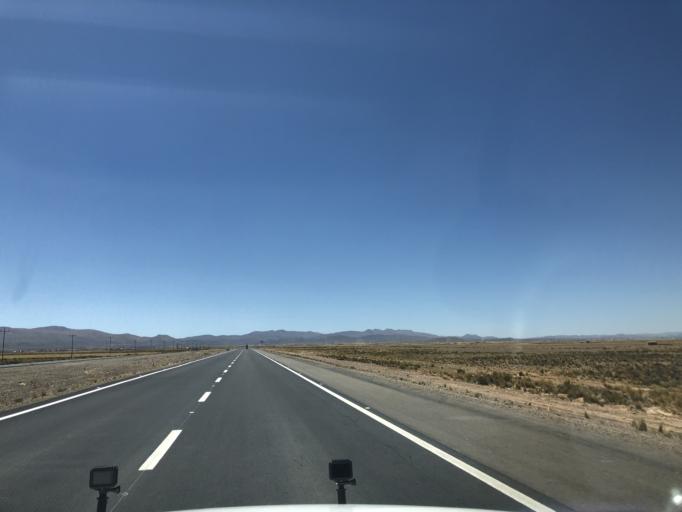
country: BO
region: La Paz
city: Colquiri
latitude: -17.6511
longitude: -67.1767
